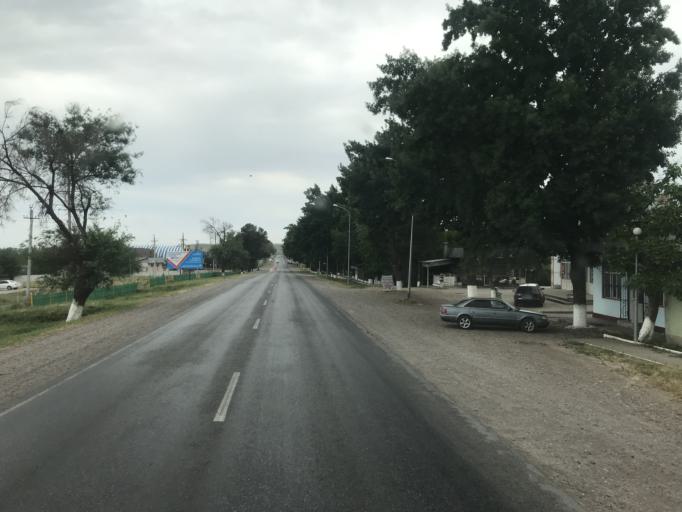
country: KZ
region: Ongtustik Qazaqstan
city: Saryaghash
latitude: 41.4911
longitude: 69.2816
